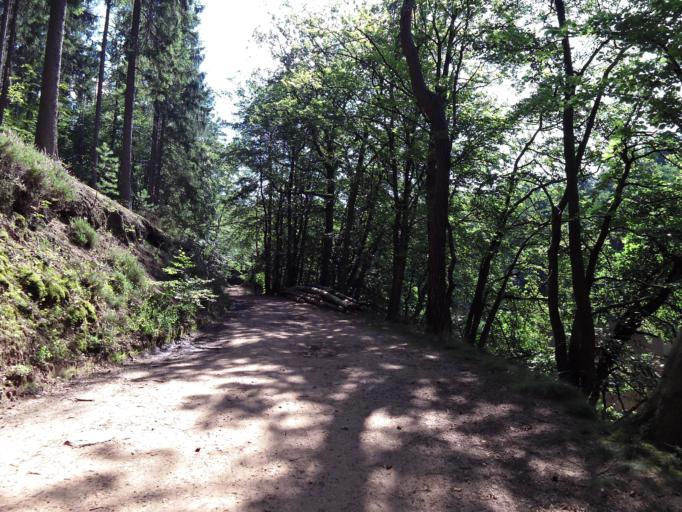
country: DE
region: Rheinland-Pfalz
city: Breunigweiler
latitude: 49.5472
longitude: 7.9598
